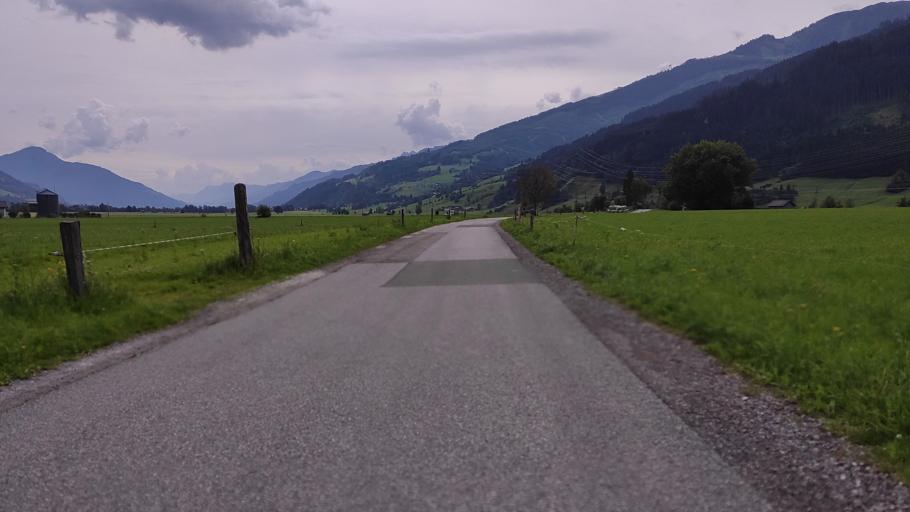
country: AT
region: Salzburg
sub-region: Politischer Bezirk Zell am See
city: Niedernsill
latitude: 47.2802
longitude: 12.6619
